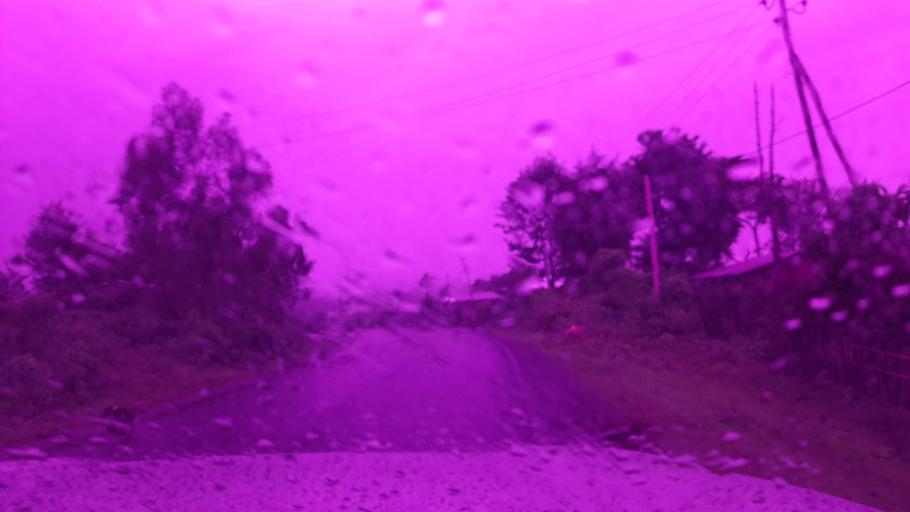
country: ET
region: Oromiya
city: Jima
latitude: 7.7190
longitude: 37.1054
